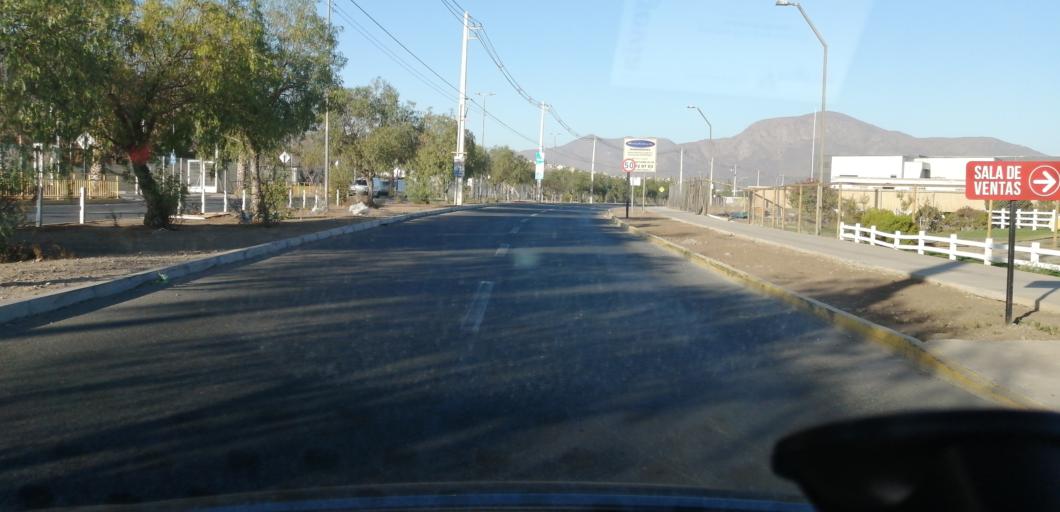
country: CL
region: Santiago Metropolitan
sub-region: Provincia de Santiago
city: Lo Prado
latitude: -33.4475
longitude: -70.8452
